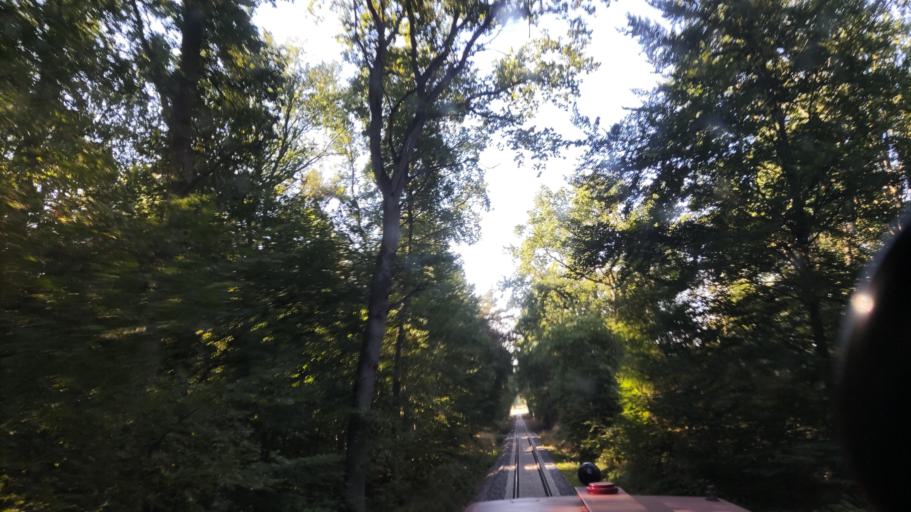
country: DE
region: Lower Saxony
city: Melbeck
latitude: 53.2042
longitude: 10.3799
